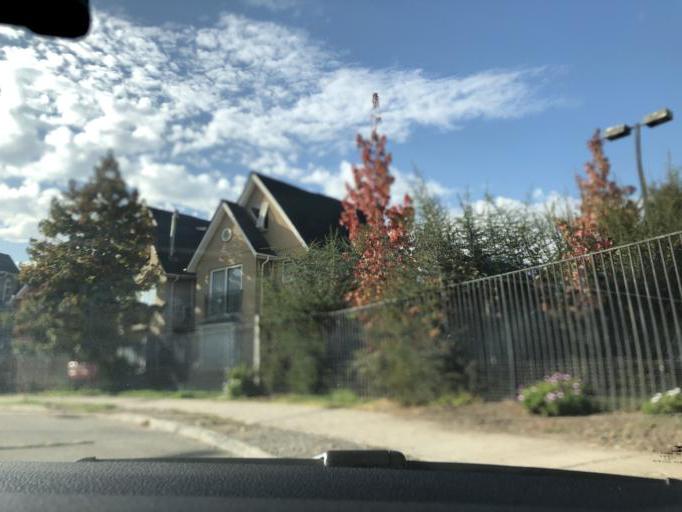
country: CL
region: Santiago Metropolitan
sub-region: Provincia de Cordillera
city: Puente Alto
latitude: -33.6022
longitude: -70.5155
